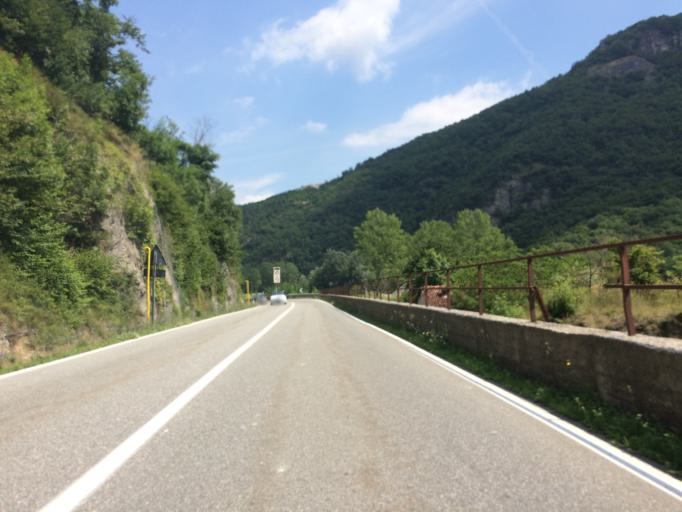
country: IT
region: Piedmont
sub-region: Provincia di Cuneo
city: Bagnasco
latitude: 44.2754
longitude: 8.0337
